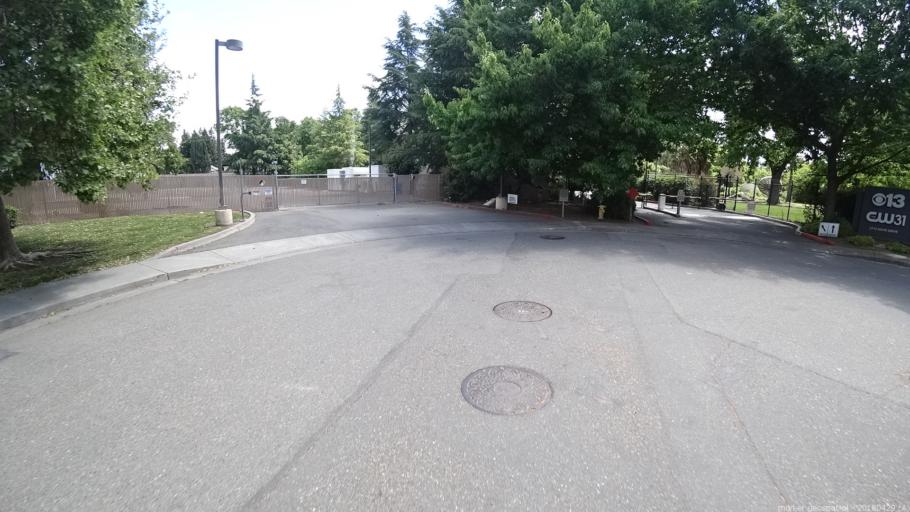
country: US
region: California
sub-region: Yolo County
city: West Sacramento
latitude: 38.5935
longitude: -121.5472
